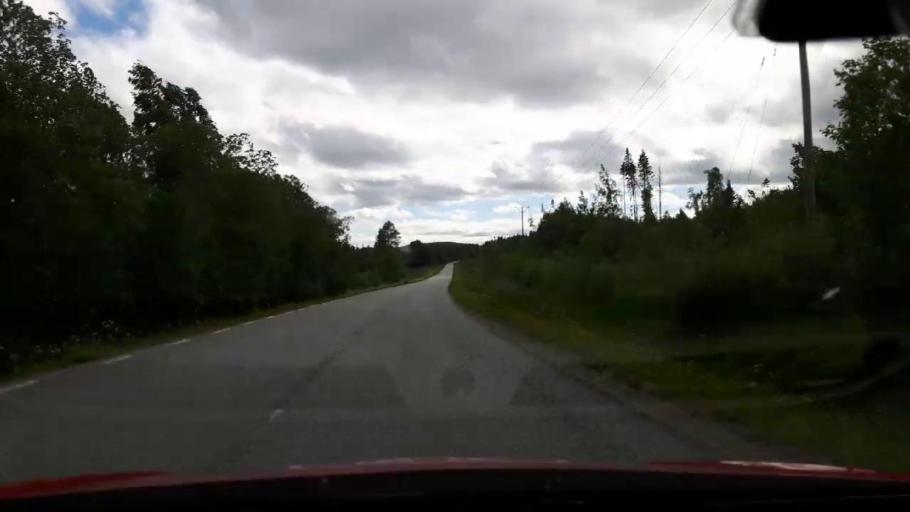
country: SE
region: Jaemtland
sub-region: Ragunda Kommun
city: Hammarstrand
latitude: 62.9708
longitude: 16.0657
